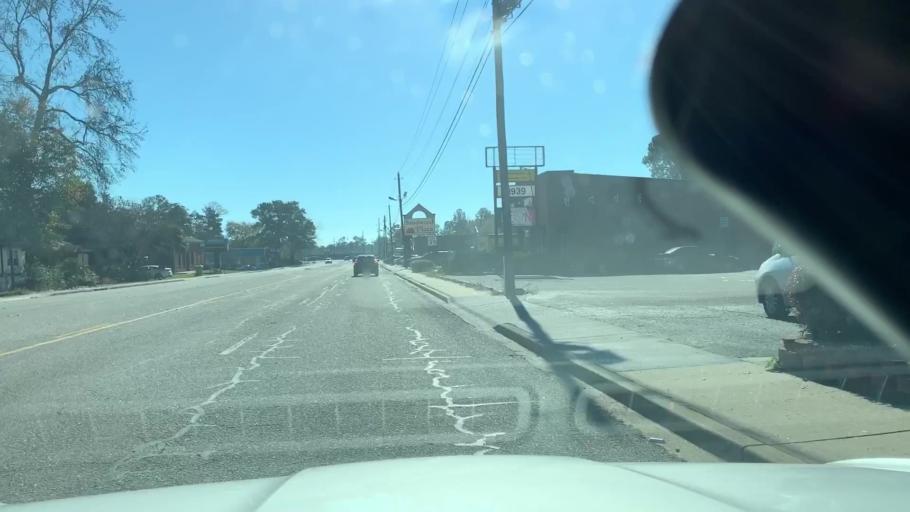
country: US
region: South Carolina
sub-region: Richland County
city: Woodfield
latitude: 34.0480
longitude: -80.9437
